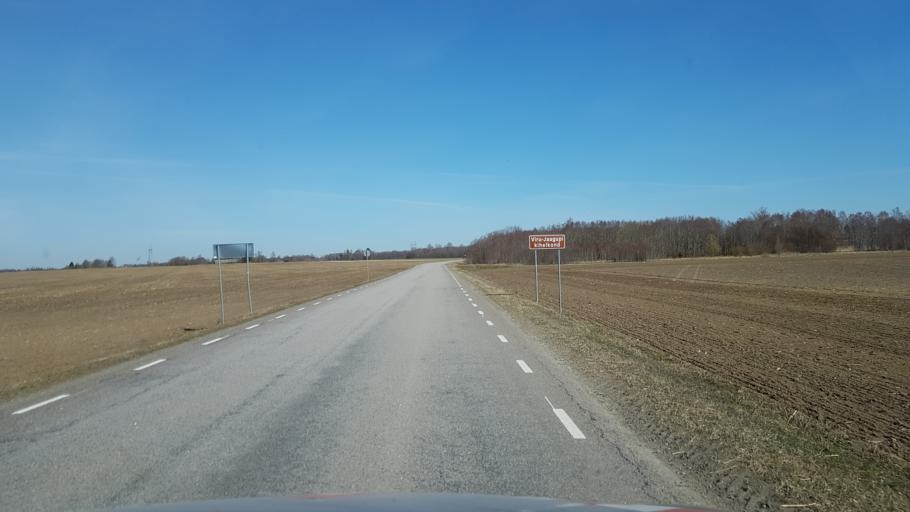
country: EE
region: Laeaene-Virumaa
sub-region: Vinni vald
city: Vinni
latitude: 59.2322
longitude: 26.3423
